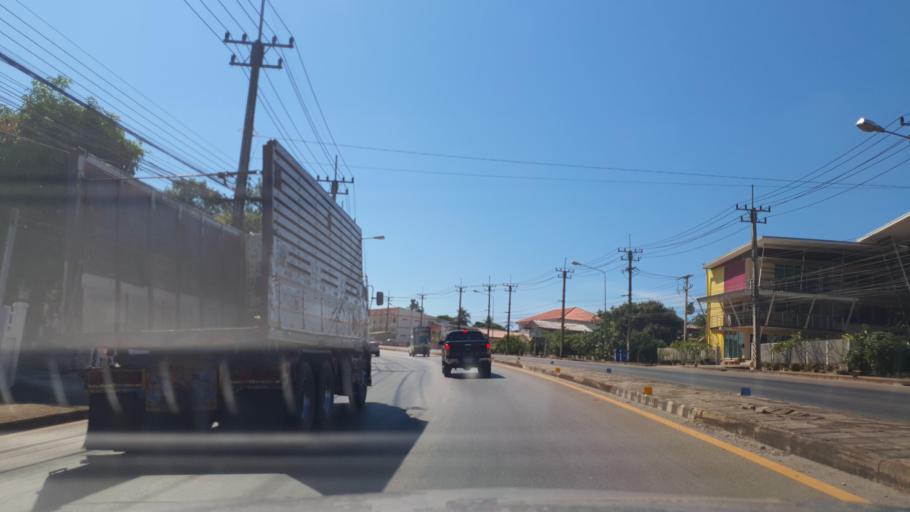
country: TH
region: Sakon Nakhon
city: Sakon Nakhon
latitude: 17.1874
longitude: 104.0930
